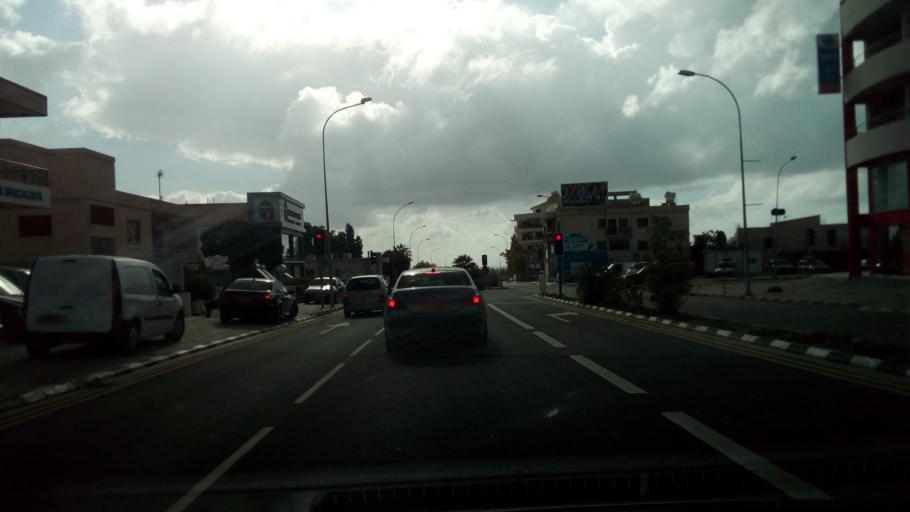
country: CY
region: Pafos
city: Paphos
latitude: 34.7742
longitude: 32.4426
